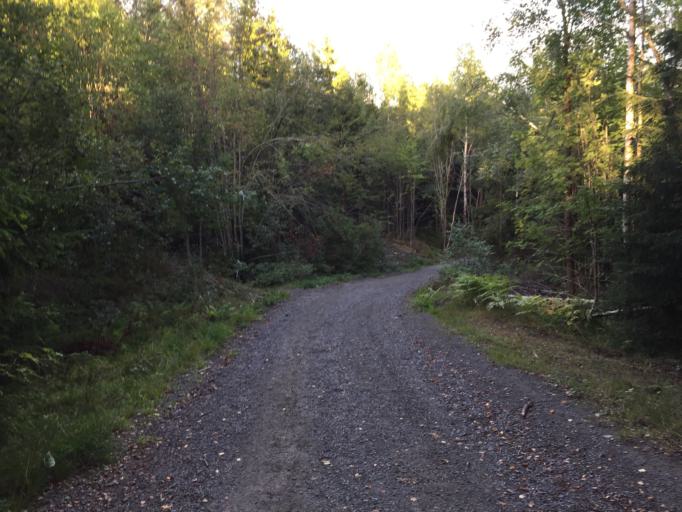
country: NO
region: Akershus
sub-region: Raelingen
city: Fjerdingby
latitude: 59.9294
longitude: 11.0457
